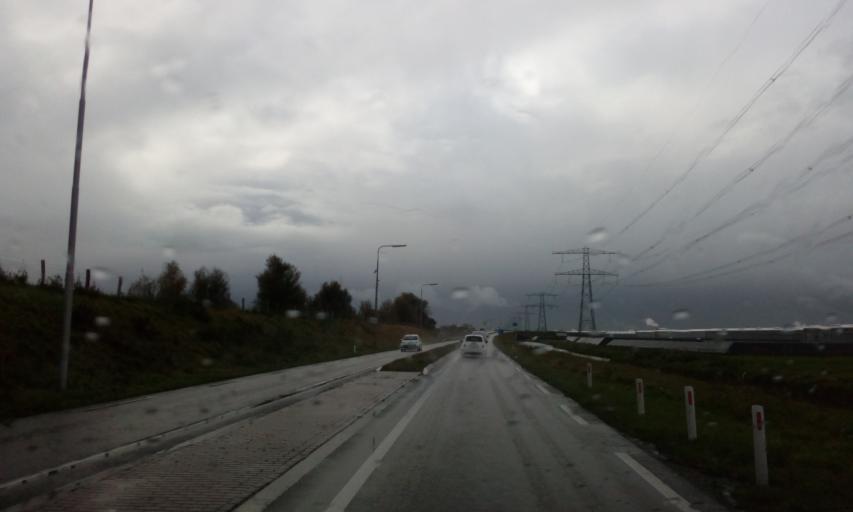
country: NL
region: South Holland
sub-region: Gemeente Westland
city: Kwintsheul
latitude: 52.0072
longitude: 4.2866
